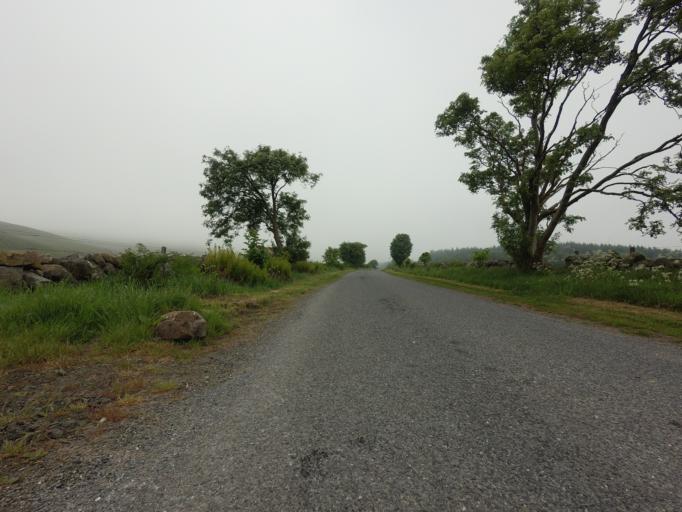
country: GB
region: Scotland
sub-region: Perth and Kinross
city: Kinross
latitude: 56.1599
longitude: -3.4530
